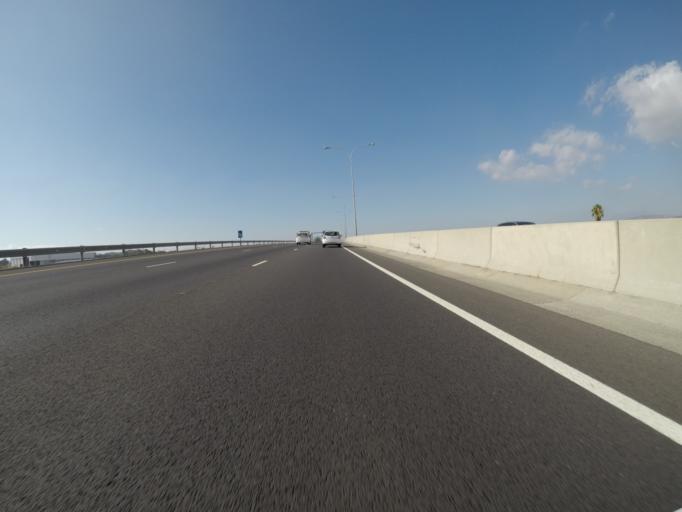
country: ZA
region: Western Cape
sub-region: City of Cape Town
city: Kraaifontein
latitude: -33.9212
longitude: 18.6645
